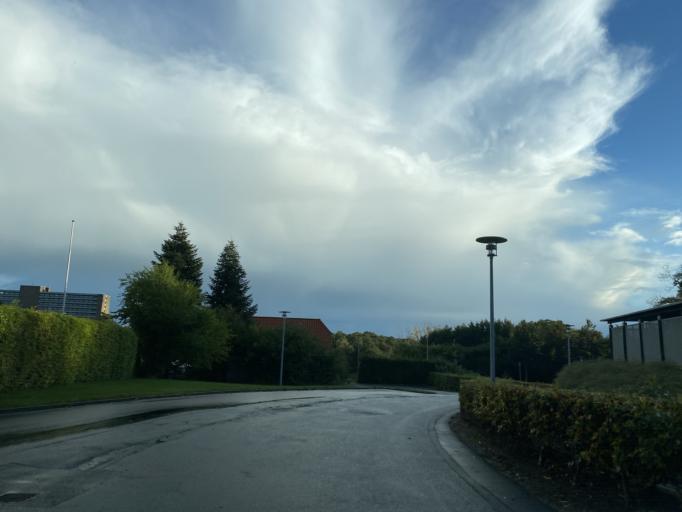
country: DK
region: South Denmark
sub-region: Haderslev Kommune
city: Haderslev
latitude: 55.2456
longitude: 9.4476
